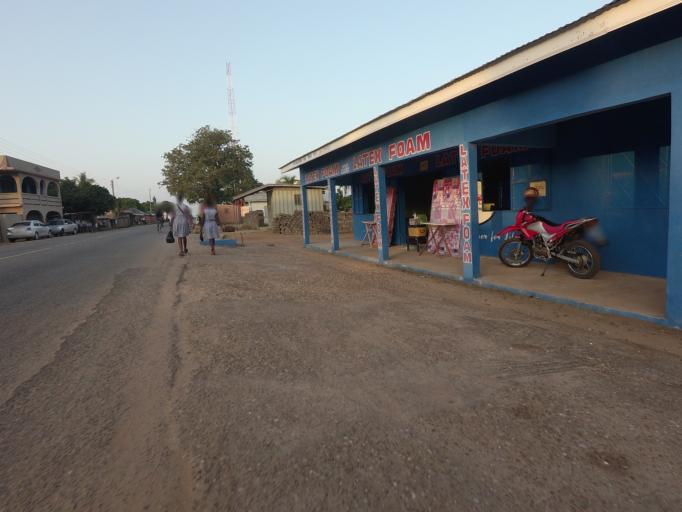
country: GH
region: Volta
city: Anloga
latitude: 5.7959
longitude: 0.9041
